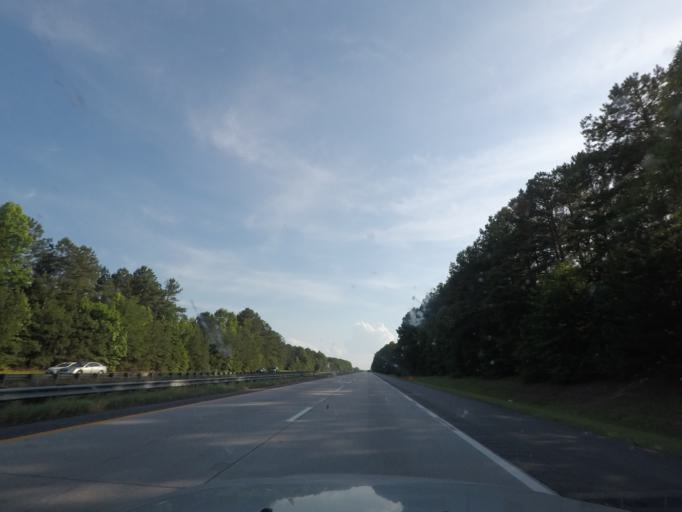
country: US
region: North Carolina
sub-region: Granville County
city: Oxford
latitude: 36.2480
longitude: -78.6268
